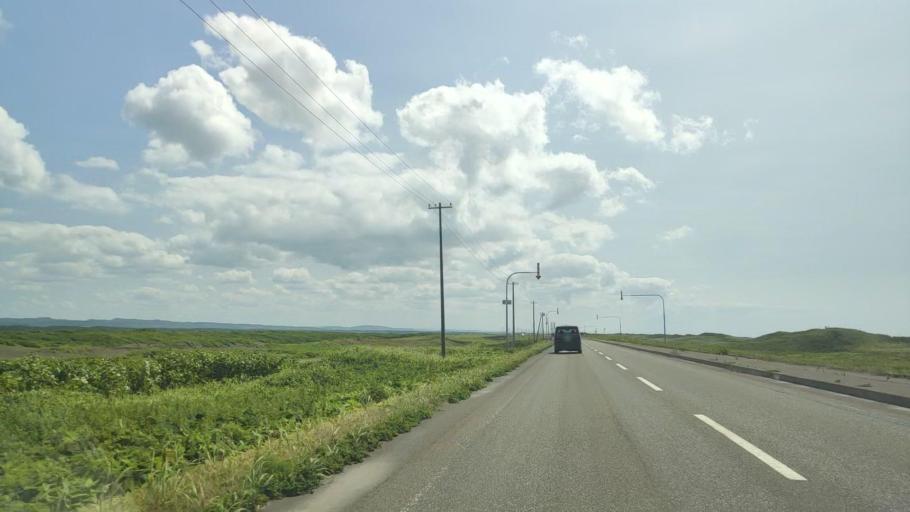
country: JP
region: Hokkaido
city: Makubetsu
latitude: 44.9523
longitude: 141.7086
